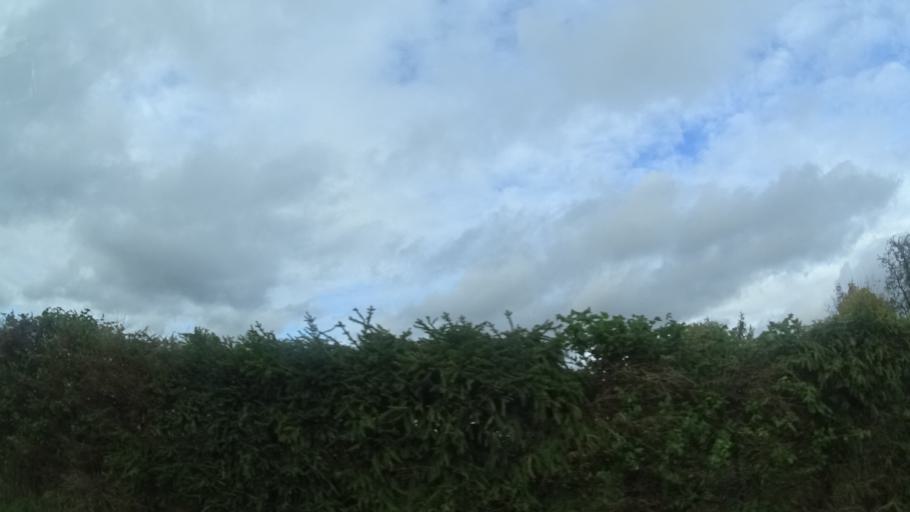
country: DE
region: Thuringia
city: Romhild
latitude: 50.3948
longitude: 10.5314
